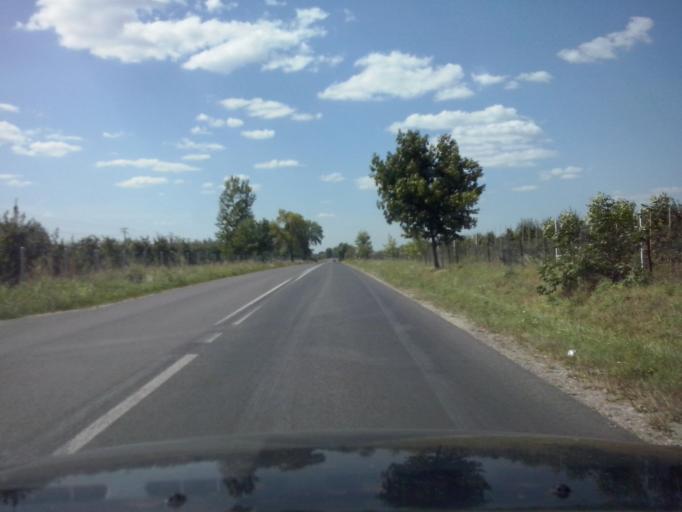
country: PL
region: Swietokrzyskie
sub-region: Powiat staszowski
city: Szydlow
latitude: 50.5870
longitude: 20.9840
